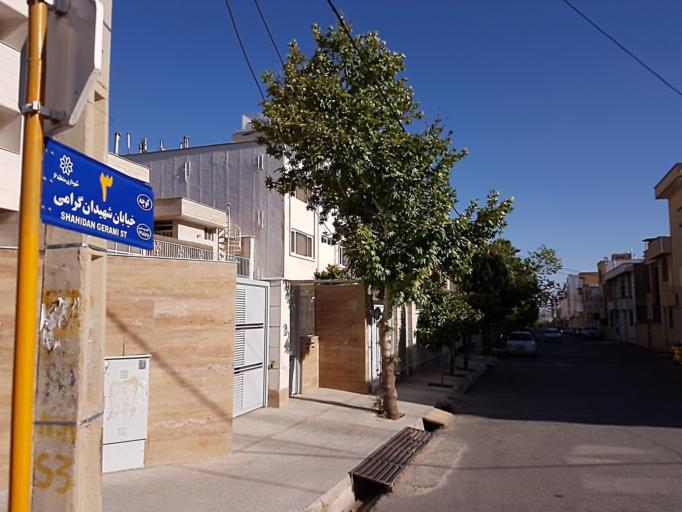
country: IR
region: Fars
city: Shiraz
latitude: 29.6704
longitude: 52.4562
